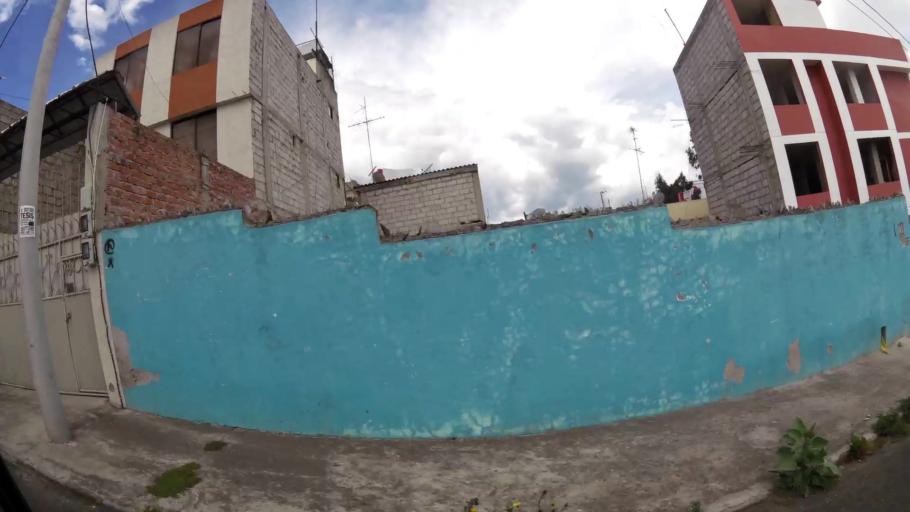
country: EC
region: Tungurahua
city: Ambato
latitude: -1.2573
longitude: -78.6169
